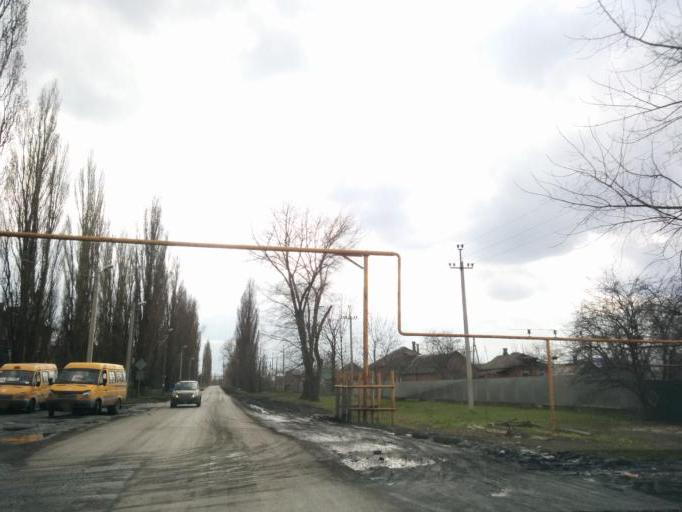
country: RU
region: Rostov
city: Shakhty
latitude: 47.6870
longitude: 40.2883
